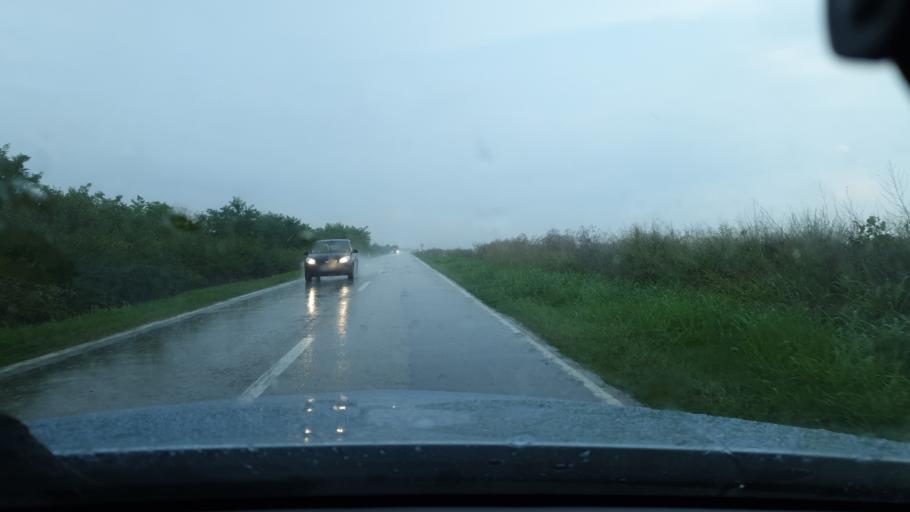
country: RS
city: Banatski Despotovac
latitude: 45.3882
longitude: 20.6065
